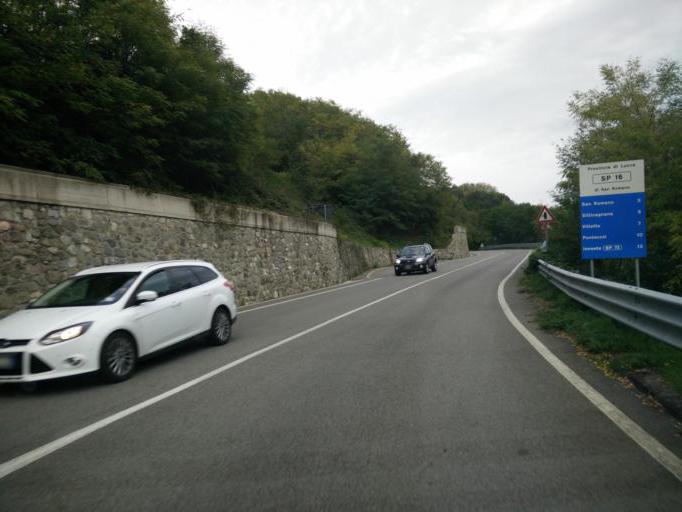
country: IT
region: Tuscany
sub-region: Provincia di Lucca
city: Piazza al Serchio-San Michele
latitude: 44.1781
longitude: 10.3105
